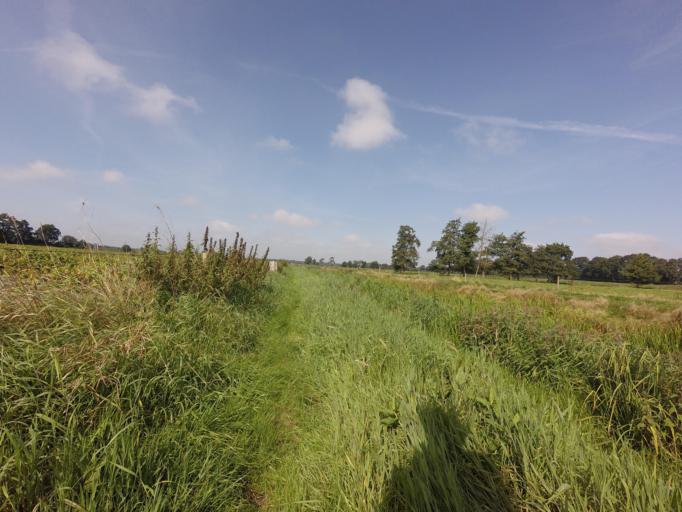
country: NL
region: Drenthe
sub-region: Gemeente Tynaarlo
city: Vries
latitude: 53.1220
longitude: 6.5437
